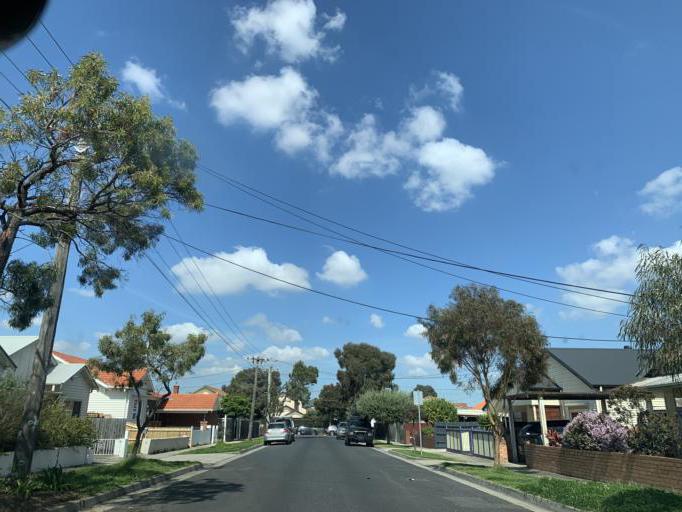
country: AU
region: Victoria
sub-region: Moreland
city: Coburg North
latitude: -37.7358
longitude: 144.9556
